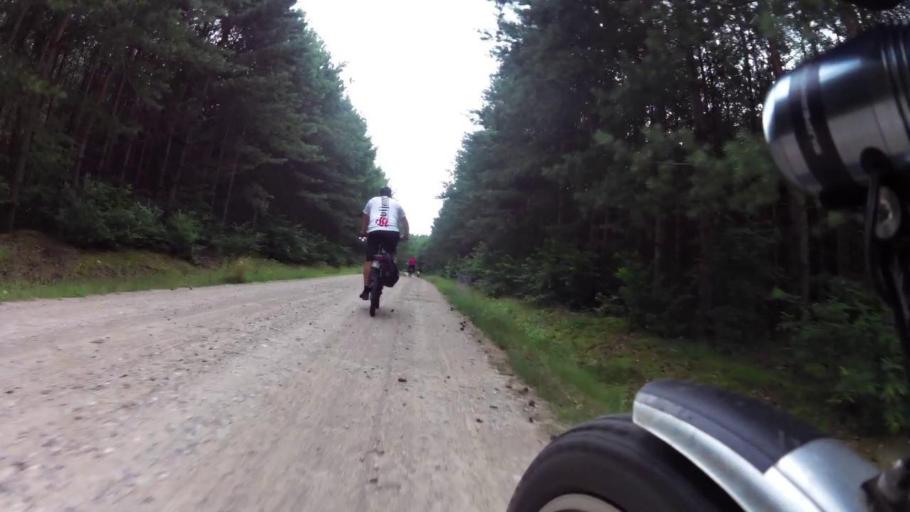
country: PL
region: West Pomeranian Voivodeship
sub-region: Powiat gryfinski
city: Mieszkowice
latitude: 52.8350
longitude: 14.5935
